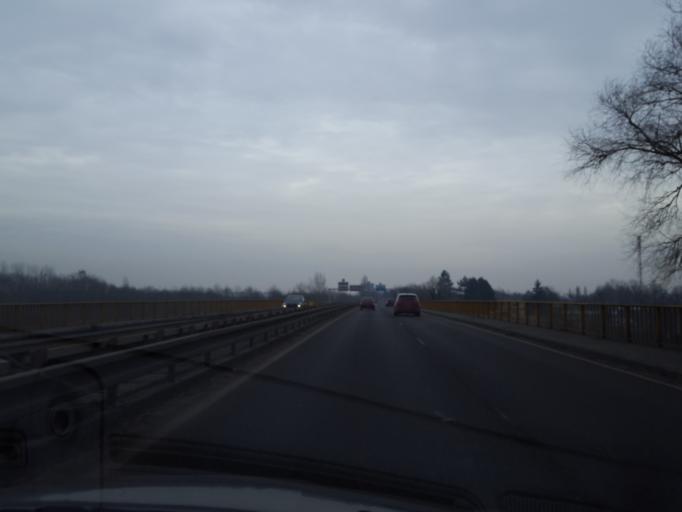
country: FR
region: Lorraine
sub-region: Departement de la Moselle
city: Moulins-les-Metz
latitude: 49.1015
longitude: 6.1128
